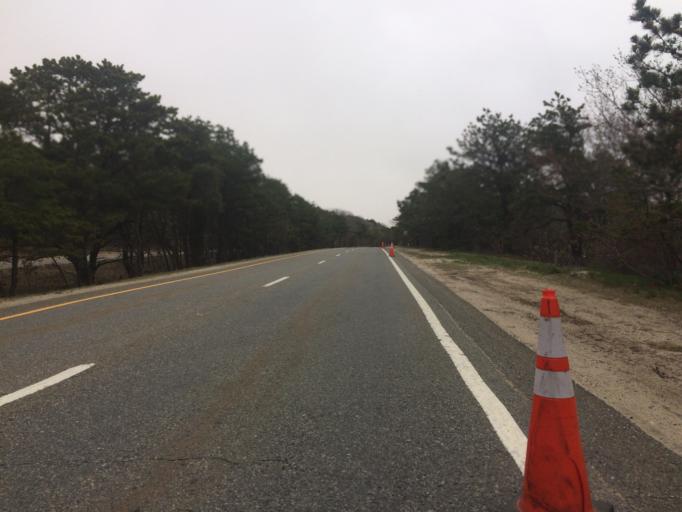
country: US
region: Massachusetts
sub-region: Barnstable County
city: Provincetown
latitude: 42.0649
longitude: -70.1699
